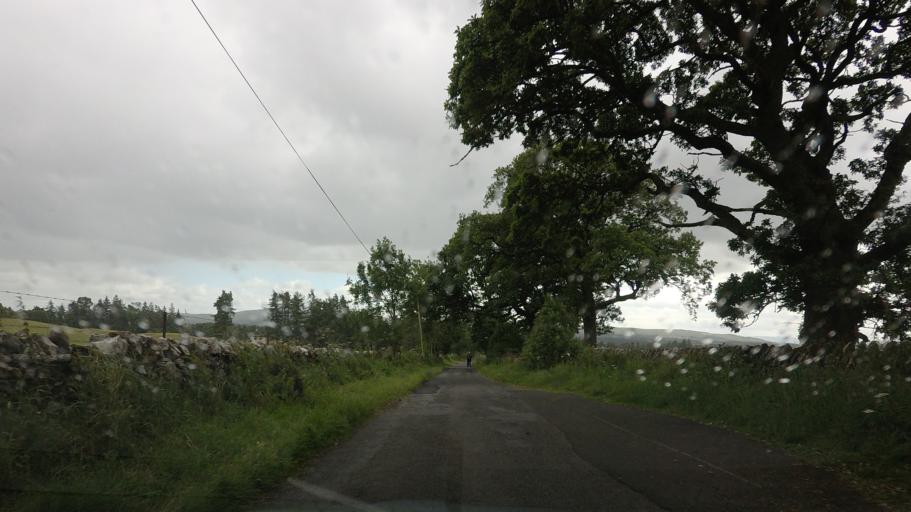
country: GB
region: Scotland
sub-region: Stirling
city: Killearn
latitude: 56.0760
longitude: -4.4500
